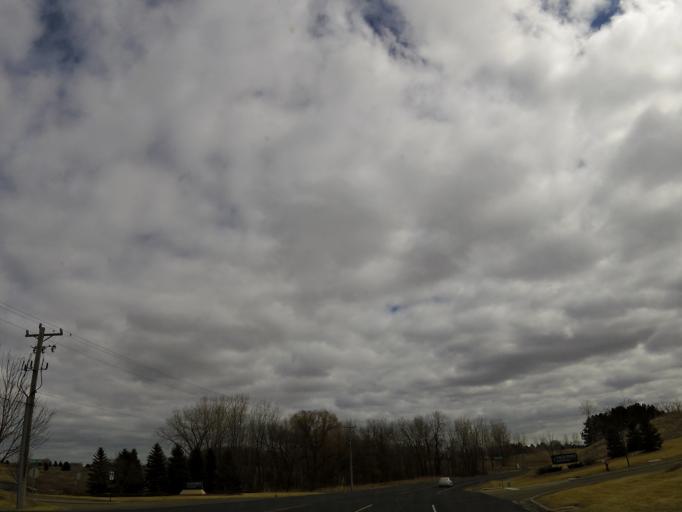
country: US
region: Minnesota
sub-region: Washington County
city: Oakdale
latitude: 44.9524
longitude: -92.9305
